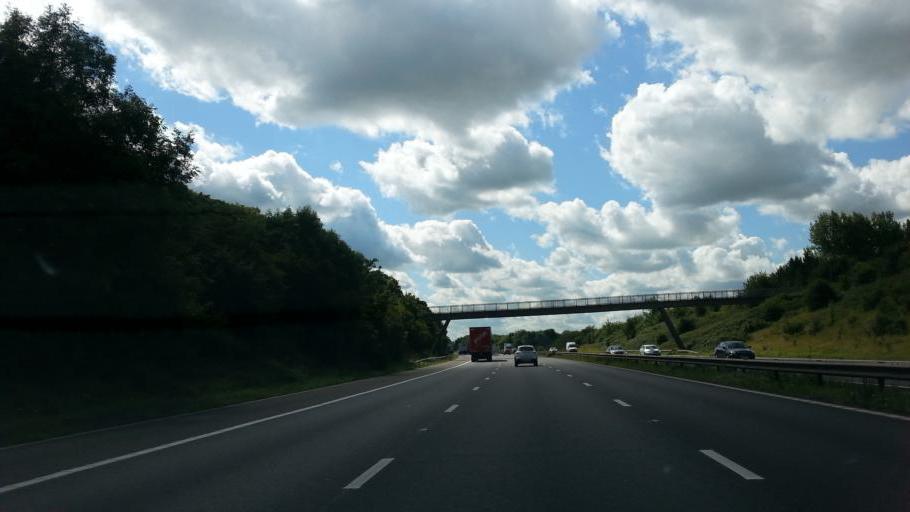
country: GB
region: England
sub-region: Leicestershire
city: Enderby
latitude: 52.5832
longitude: -1.1982
